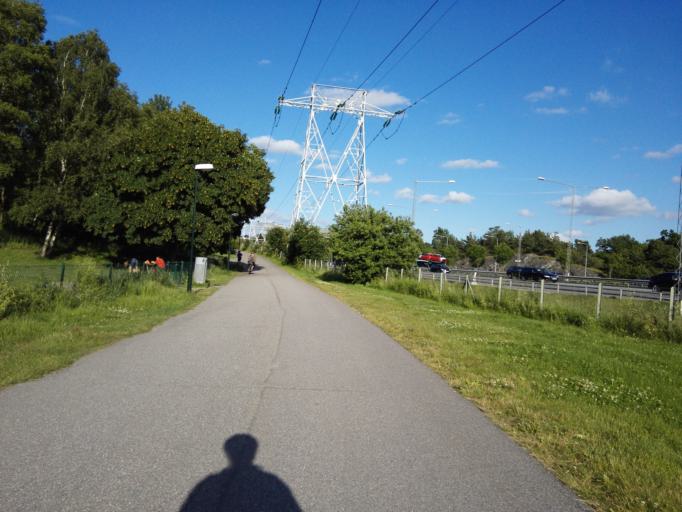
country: SE
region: Stockholm
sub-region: Huddinge Kommun
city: Huddinge
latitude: 59.2893
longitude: 17.9847
